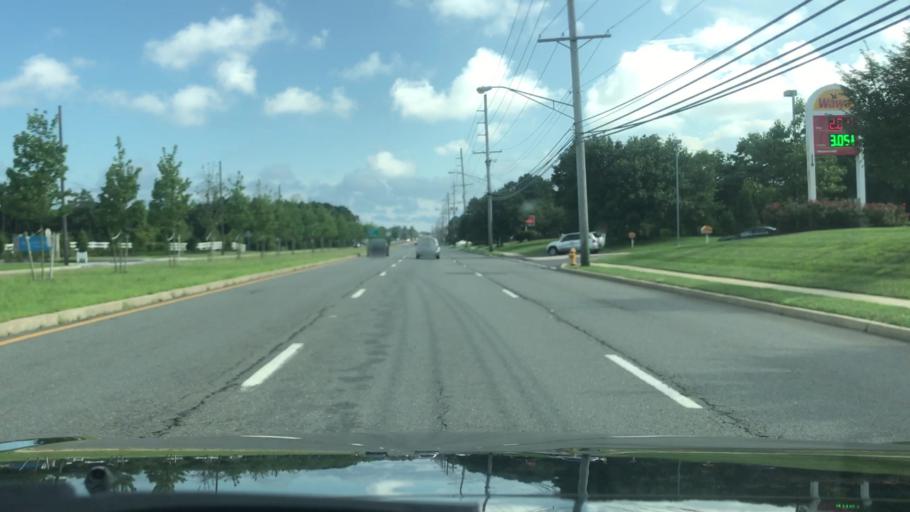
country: US
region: New Jersey
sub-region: Ocean County
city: Leisure Village East
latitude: 40.0296
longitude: -74.1438
